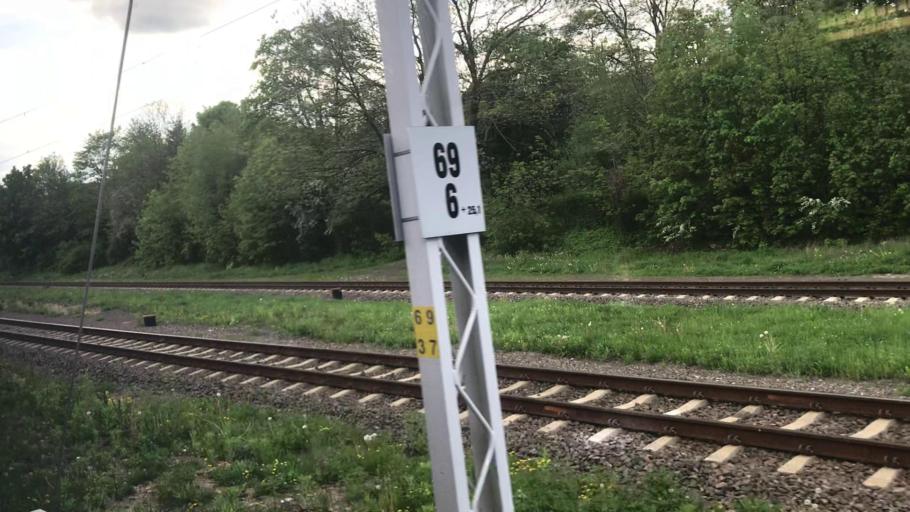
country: PL
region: Lower Silesian Voivodeship
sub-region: Powiat walbrzyski
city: Walbrzych
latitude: 50.7858
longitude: 16.2852
